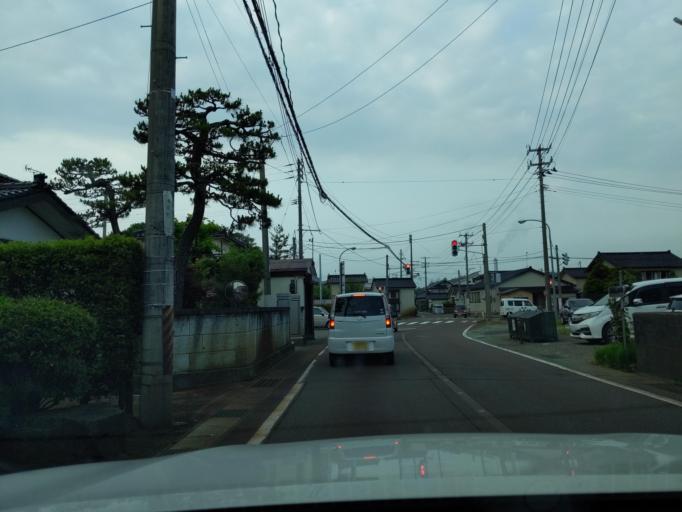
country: JP
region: Niigata
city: Kashiwazaki
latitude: 37.3878
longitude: 138.5787
